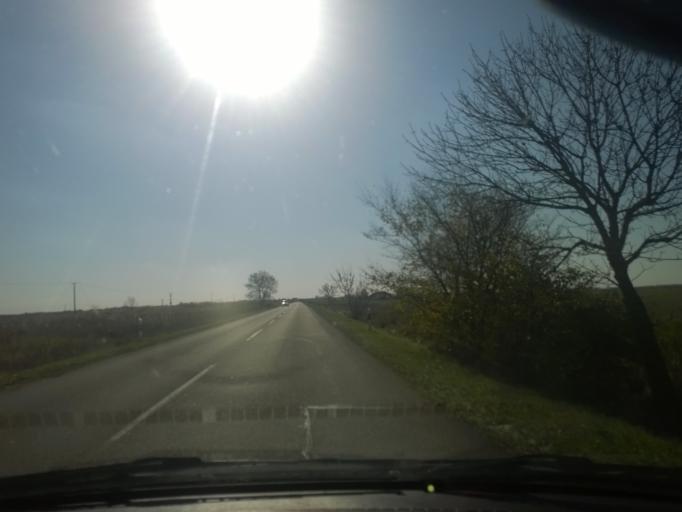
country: HU
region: Csongrad
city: Hodmezovasarhely
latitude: 46.5211
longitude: 20.3121
